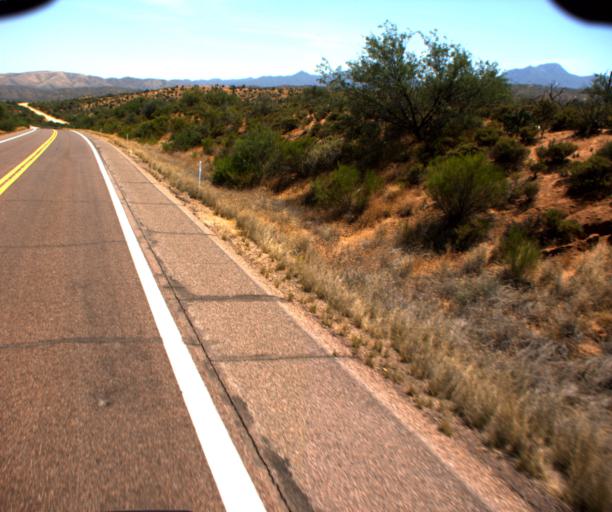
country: US
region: Arizona
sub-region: Gila County
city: Tonto Basin
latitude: 33.7922
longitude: -111.2673
